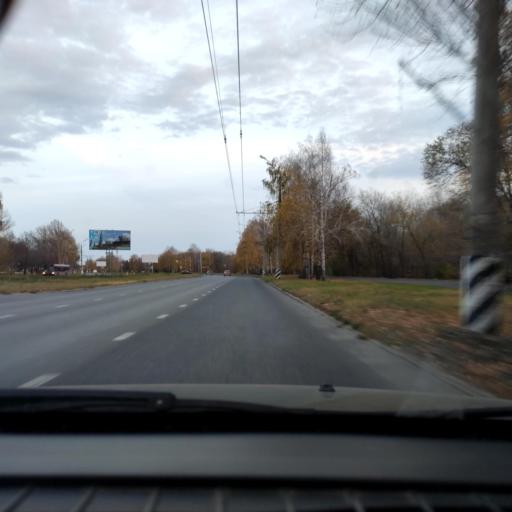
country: RU
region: Samara
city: Tol'yatti
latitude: 53.5011
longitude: 49.2644
